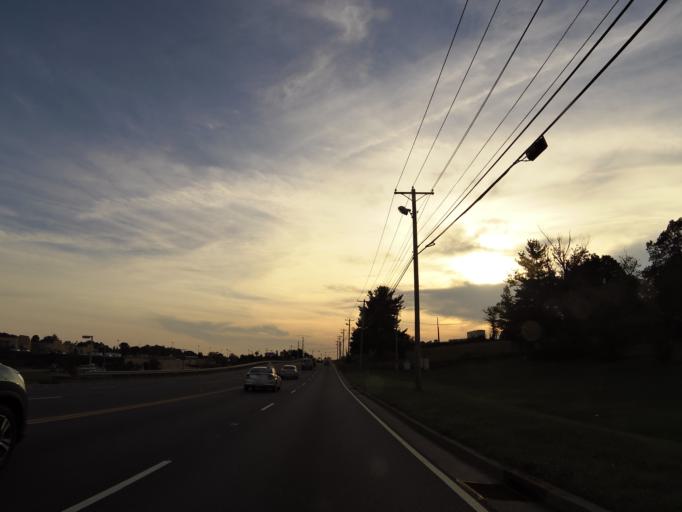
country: US
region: Tennessee
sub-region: Blount County
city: Maryville
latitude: 35.7190
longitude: -84.0106
